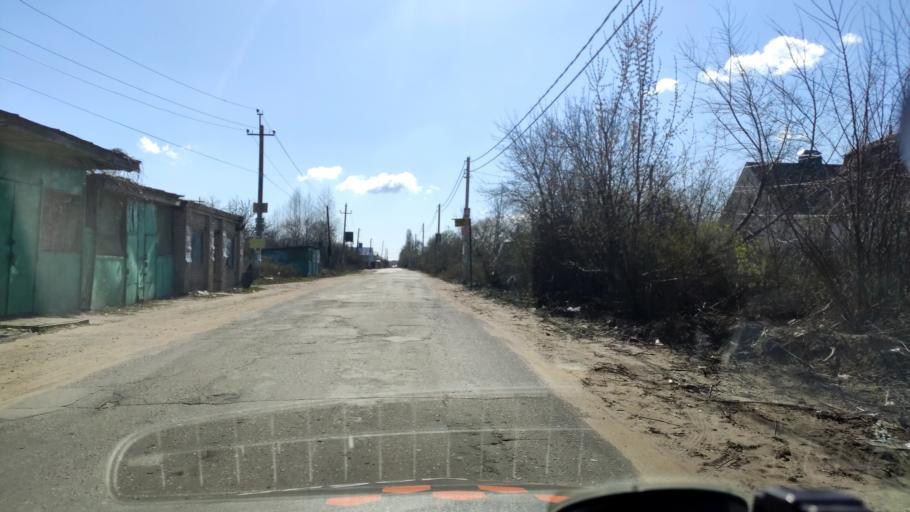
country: RU
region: Voronezj
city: Shilovo
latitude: 51.5944
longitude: 39.1539
